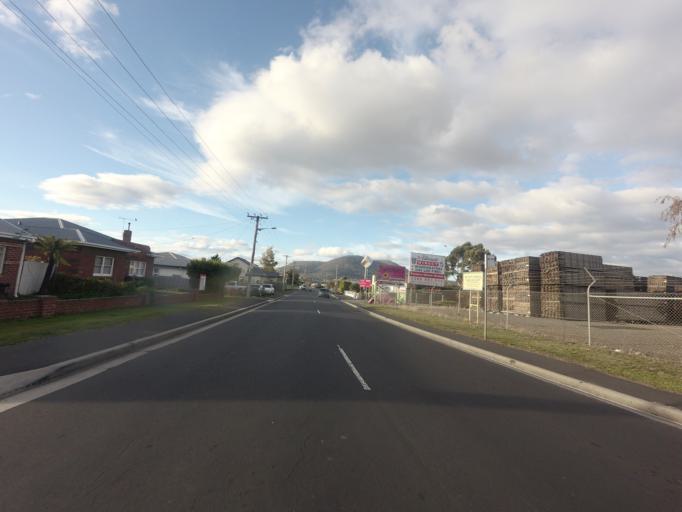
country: AU
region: Tasmania
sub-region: Glenorchy
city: Glenorchy
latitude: -42.8276
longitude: 147.2711
